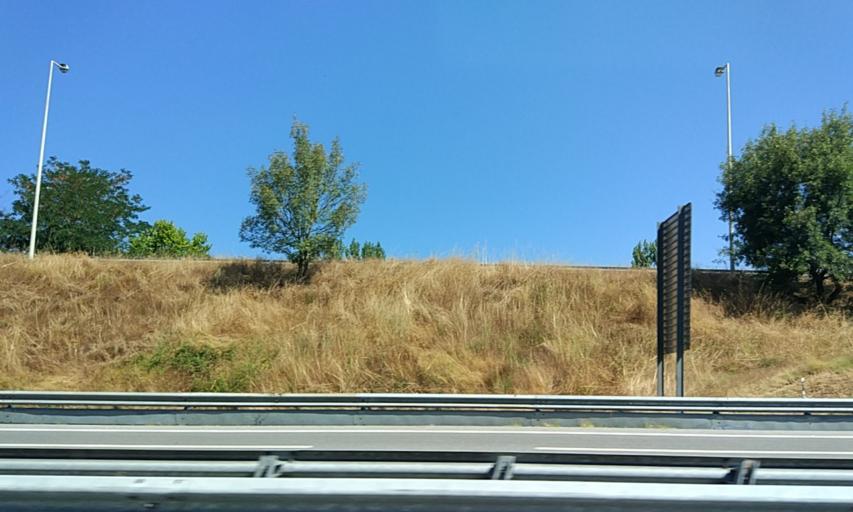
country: PT
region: Porto
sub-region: Lousada
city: Meinedo
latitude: 41.2312
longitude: -8.2060
